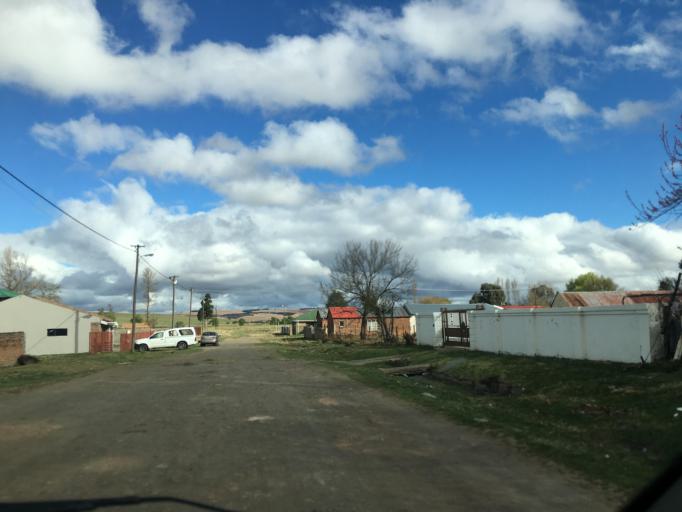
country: ZA
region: Eastern Cape
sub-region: Chris Hani District Municipality
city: Elliot
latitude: -31.3357
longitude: 27.8520
